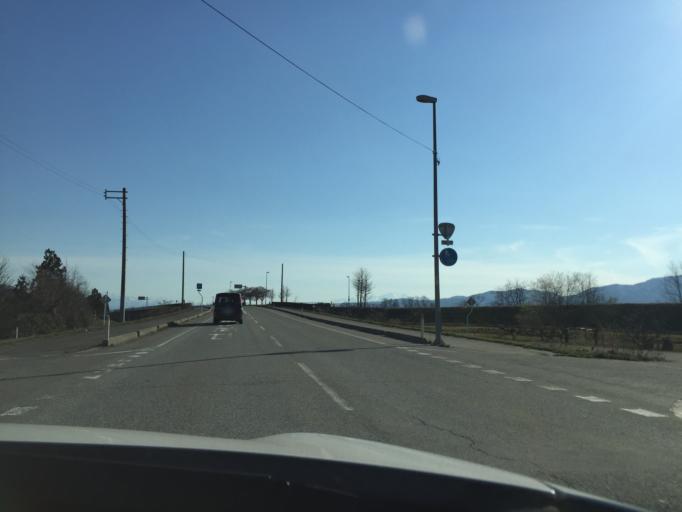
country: JP
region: Yamagata
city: Nagai
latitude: 38.1388
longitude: 140.0568
